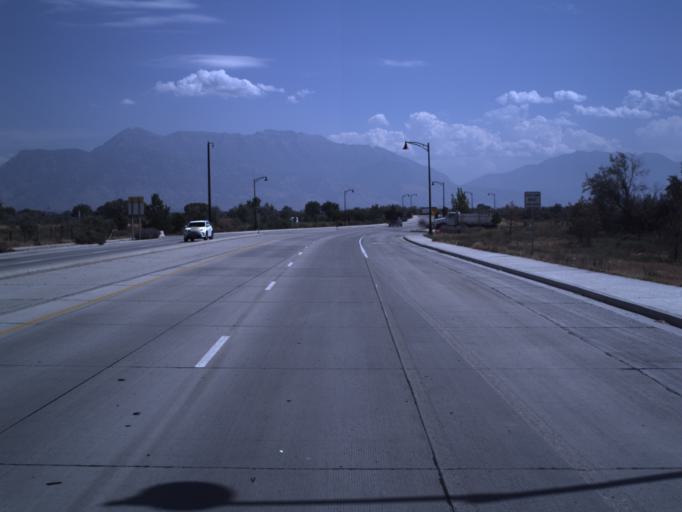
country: US
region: Utah
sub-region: Utah County
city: Saratoga Springs
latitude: 40.3727
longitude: -111.9125
